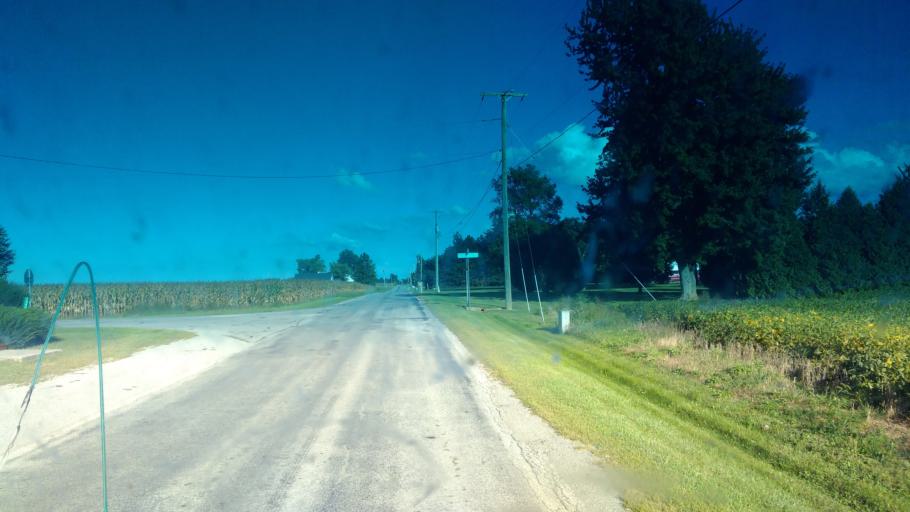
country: US
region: Ohio
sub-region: Hancock County
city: Arlington
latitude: 40.9356
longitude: -83.6238
